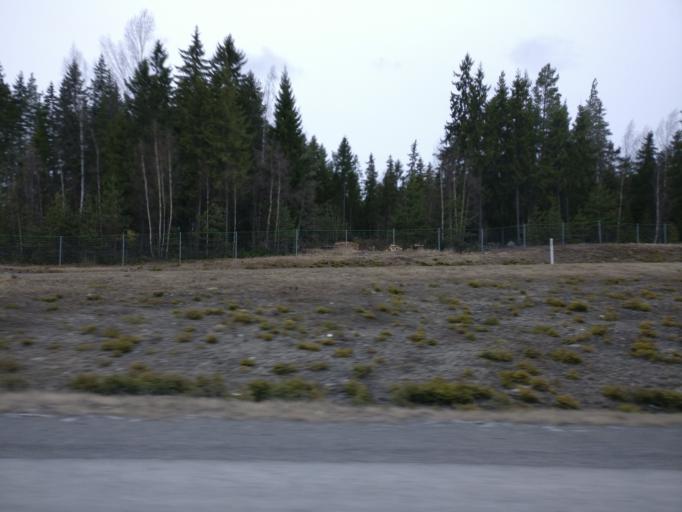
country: FI
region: Pirkanmaa
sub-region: Tampere
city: Lempaeaelae
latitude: 61.2915
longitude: 23.8137
